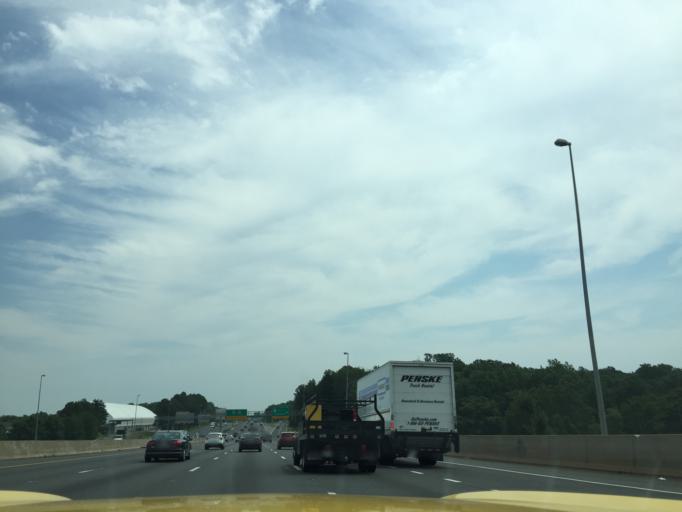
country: US
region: Virginia
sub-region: Fairfax County
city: Franconia
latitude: 38.7944
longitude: -77.1466
